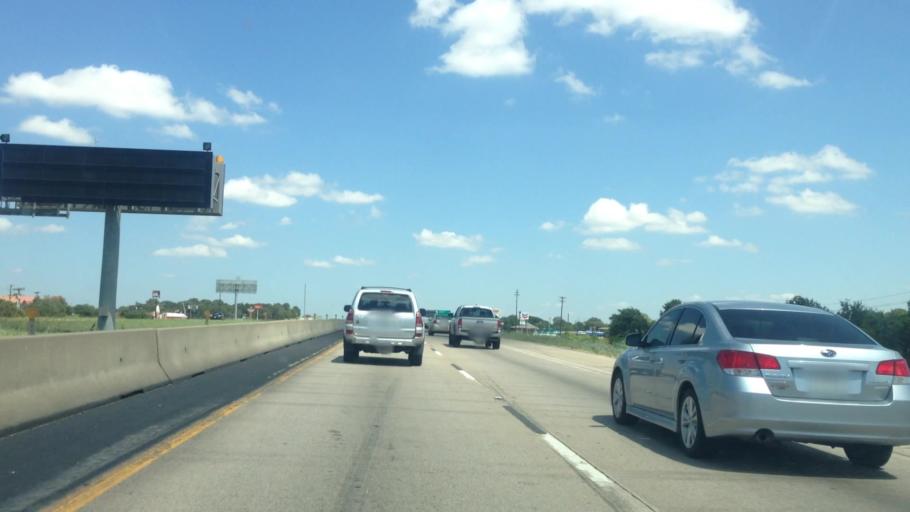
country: US
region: Texas
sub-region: Tarrant County
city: Bedford
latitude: 32.8491
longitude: -97.1125
